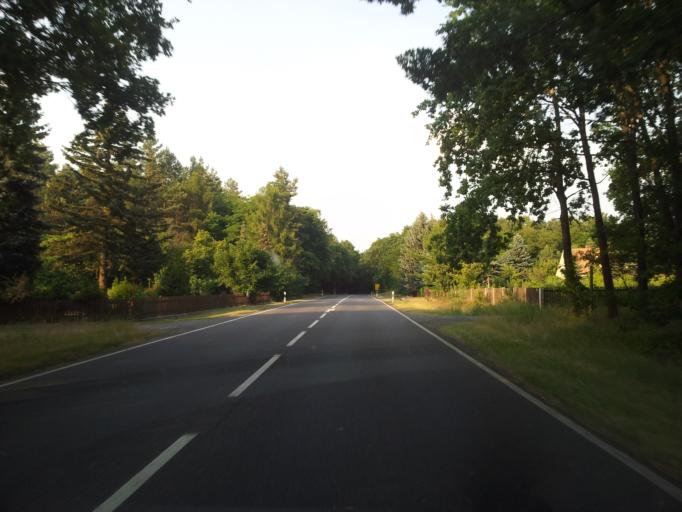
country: DE
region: Saxony
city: Bernsdorf
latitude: 51.3896
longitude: 14.0940
